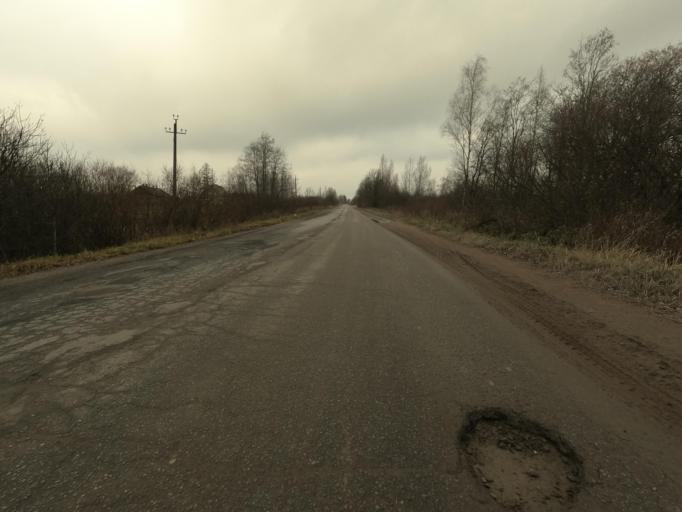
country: RU
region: Leningrad
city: Lyuban'
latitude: 59.4812
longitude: 31.2616
